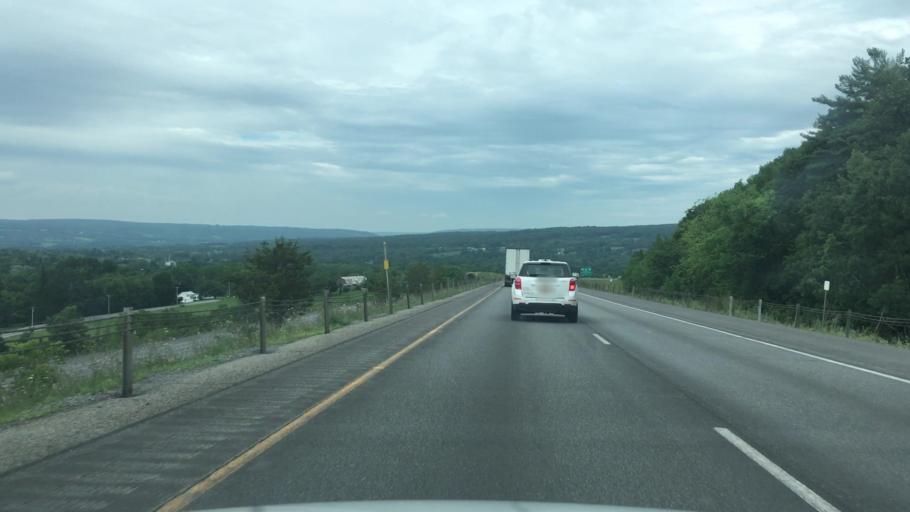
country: US
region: New York
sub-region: Schoharie County
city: Schoharie
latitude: 42.6974
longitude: -74.3457
